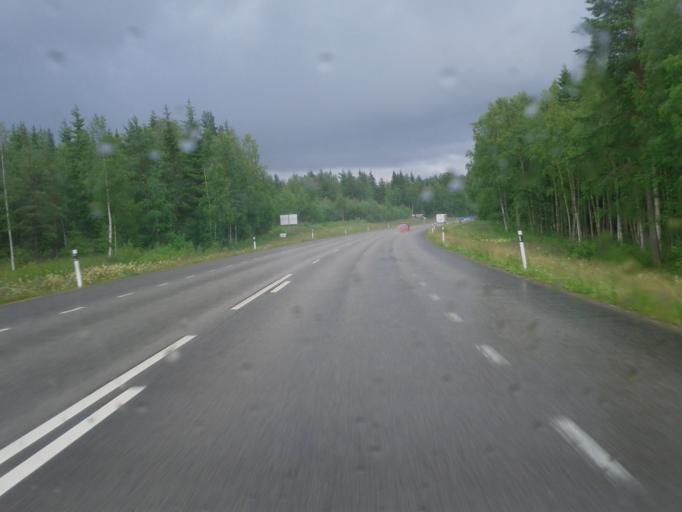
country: SE
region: Dalarna
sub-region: Rattviks Kommun
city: Vikarbyn
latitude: 60.9142
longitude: 15.0420
